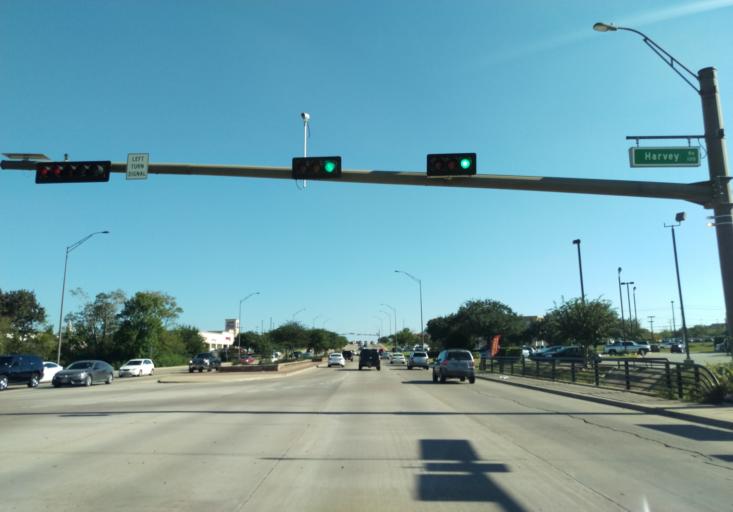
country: US
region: Texas
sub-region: Brazos County
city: College Station
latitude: 30.6151
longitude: -96.3192
